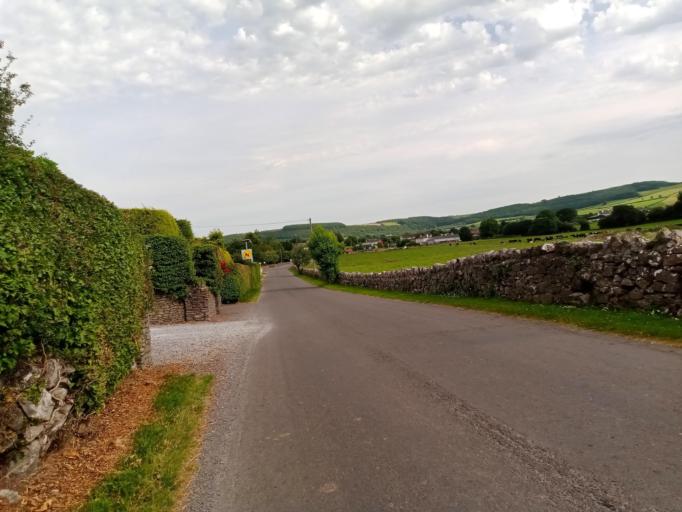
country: IE
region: Leinster
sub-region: Laois
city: Rathdowney
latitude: 52.8218
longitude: -7.4800
